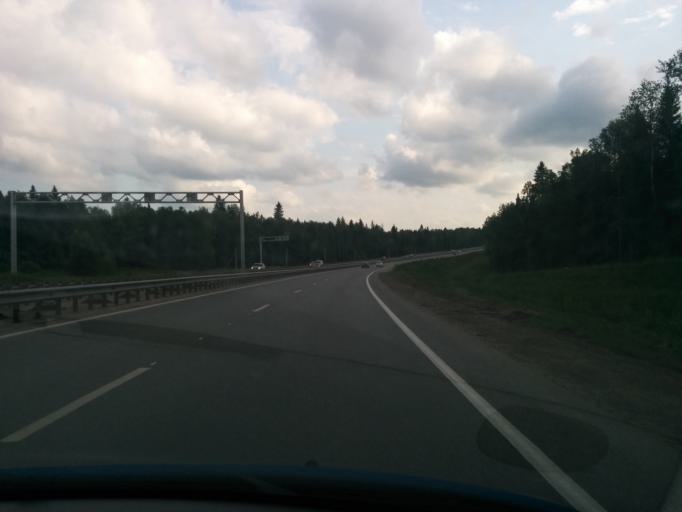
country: RU
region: Perm
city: Novyye Lyady
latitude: 58.0322
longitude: 56.4337
